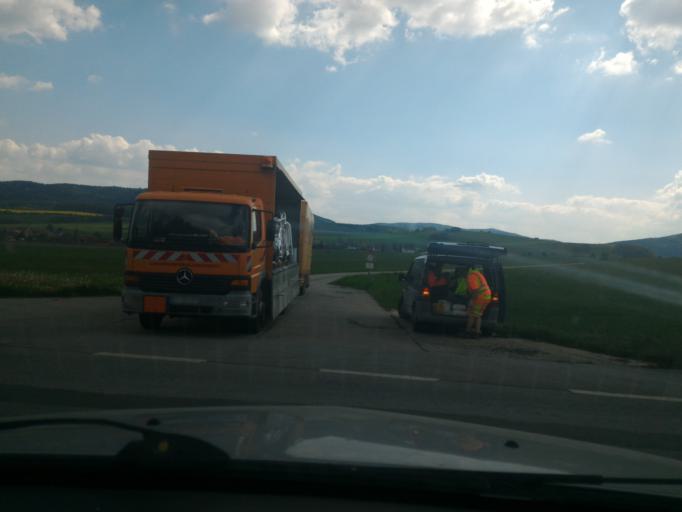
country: DE
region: Saxony
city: Bertsdorf-Hoernitz
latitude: 50.8842
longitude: 14.7111
